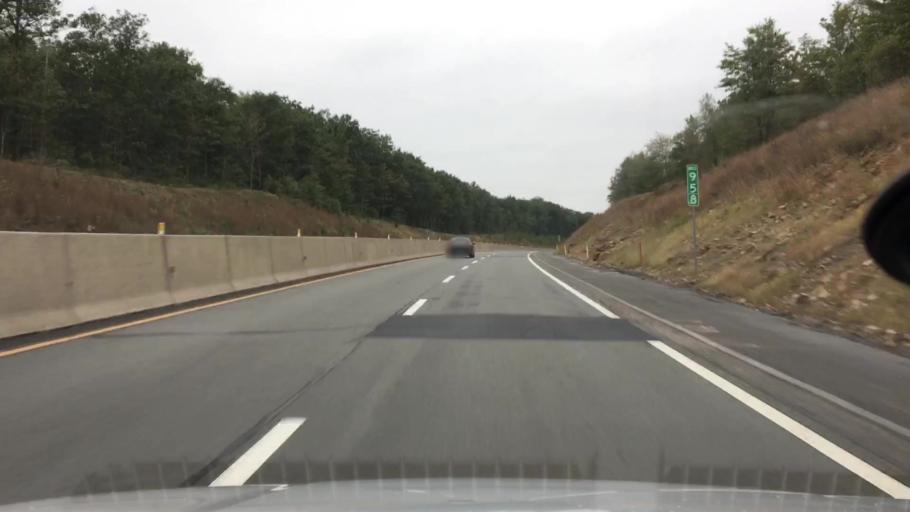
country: US
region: Pennsylvania
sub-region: Luzerne County
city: White Haven
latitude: 41.0775
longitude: -75.7263
